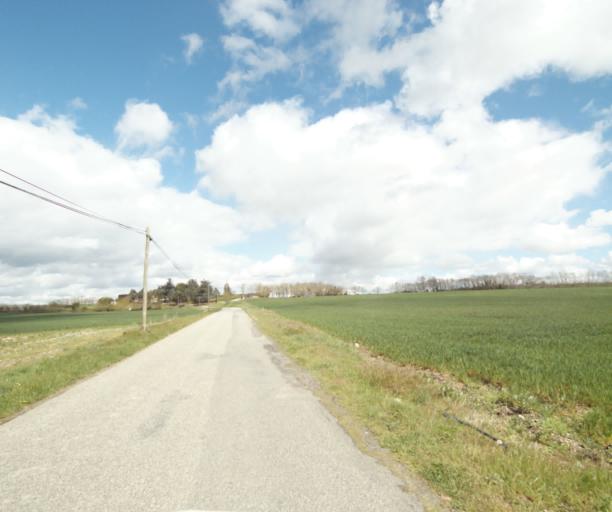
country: FR
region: Midi-Pyrenees
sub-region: Departement de l'Ariege
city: Saverdun
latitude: 43.2434
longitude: 1.5874
